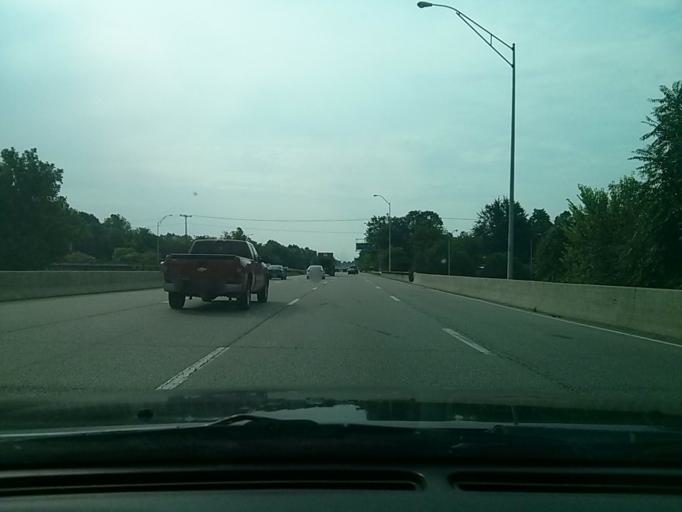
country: US
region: Oklahoma
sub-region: Tulsa County
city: Tulsa
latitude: 36.1412
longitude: -95.9552
